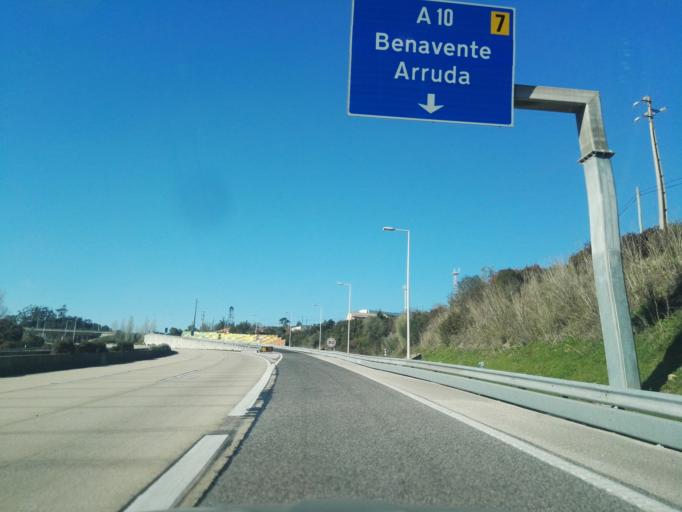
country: PT
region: Lisbon
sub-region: Vila Franca de Xira
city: Vialonga
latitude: 38.9097
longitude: -9.0684
